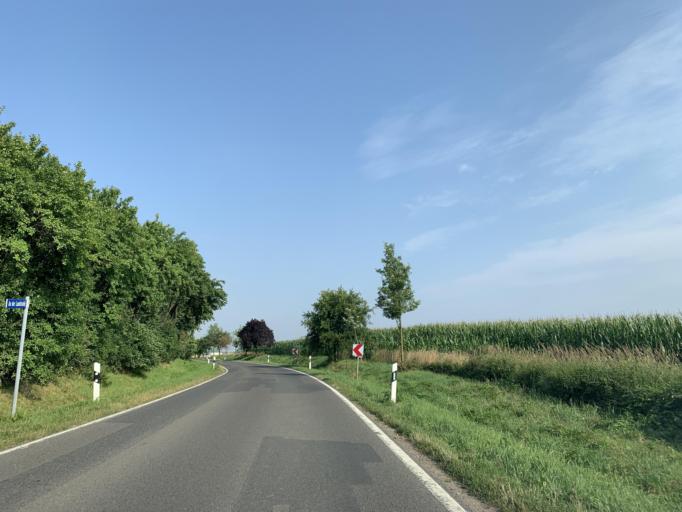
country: DE
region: Mecklenburg-Vorpommern
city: Blankensee
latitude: 53.4139
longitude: 13.2237
